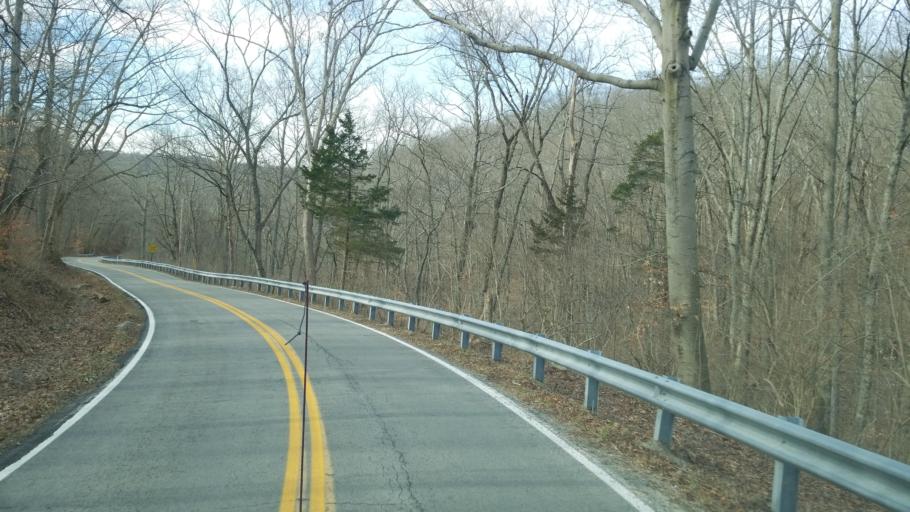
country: US
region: Ohio
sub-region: Warren County
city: Waynesville
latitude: 39.4517
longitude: -84.0899
